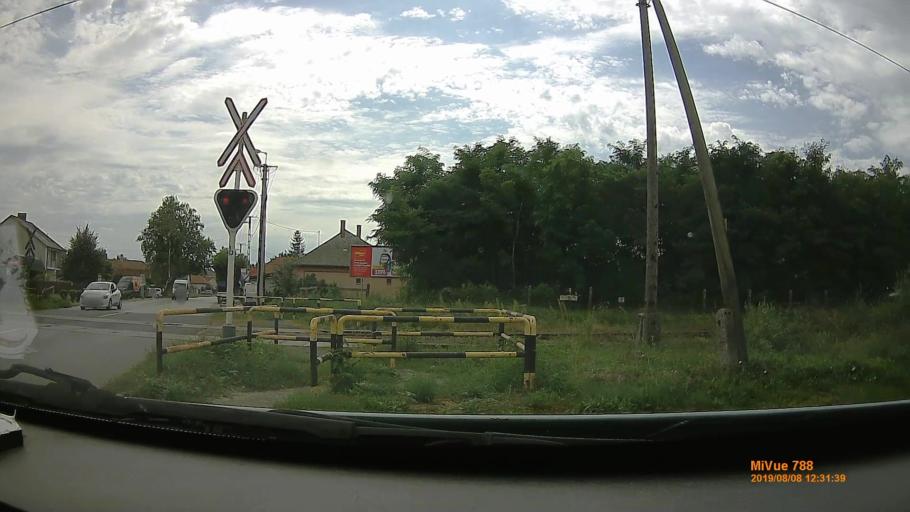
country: HU
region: Szabolcs-Szatmar-Bereg
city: Nyirbator
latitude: 47.8419
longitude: 22.1215
